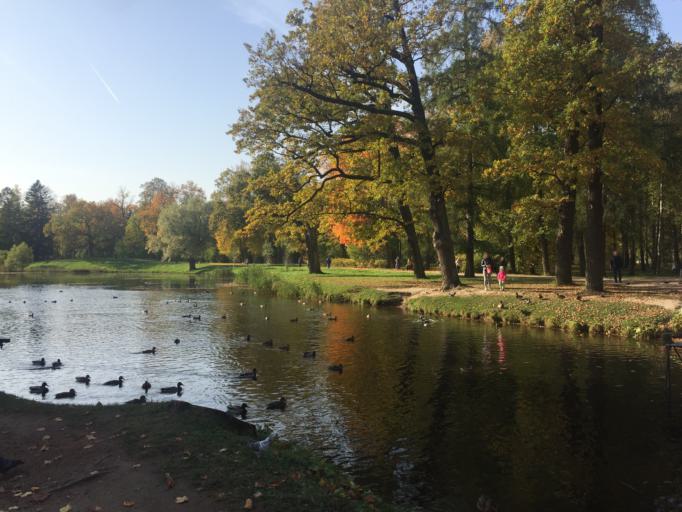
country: RU
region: St.-Petersburg
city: Pushkin
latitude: 59.7221
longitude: 30.3915
